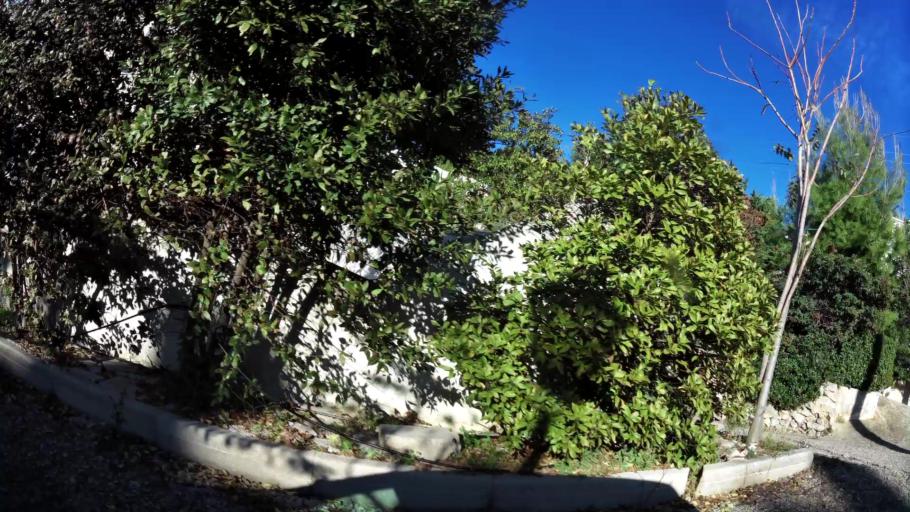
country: GR
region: Attica
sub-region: Nomarchia Athinas
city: Ekali
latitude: 38.0918
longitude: 23.8348
